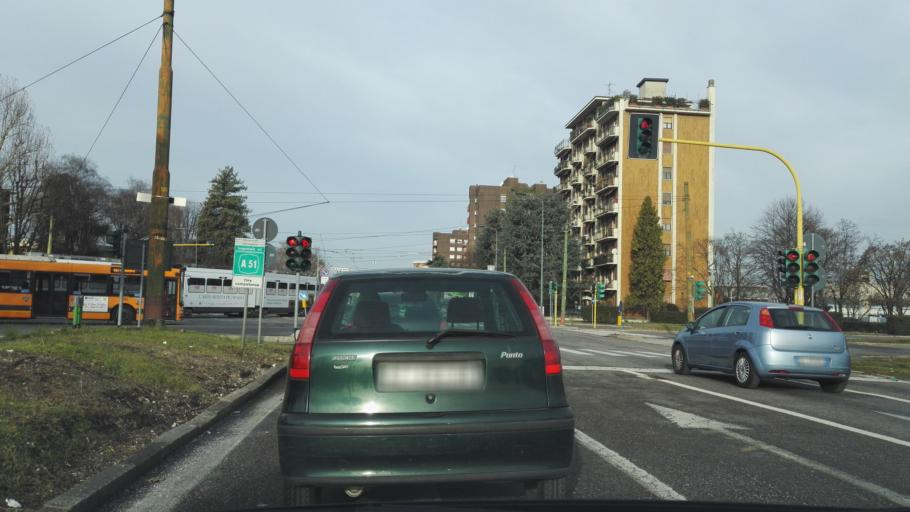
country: IT
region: Lombardy
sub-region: Citta metropolitana di Milano
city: Linate
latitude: 45.4471
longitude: 9.2560
